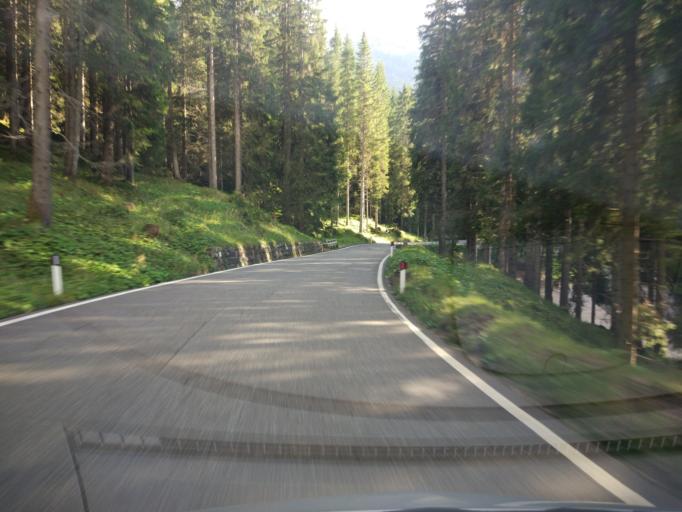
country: IT
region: Veneto
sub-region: Provincia di Belluno
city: Falcade Alto
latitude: 46.3026
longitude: 11.7582
